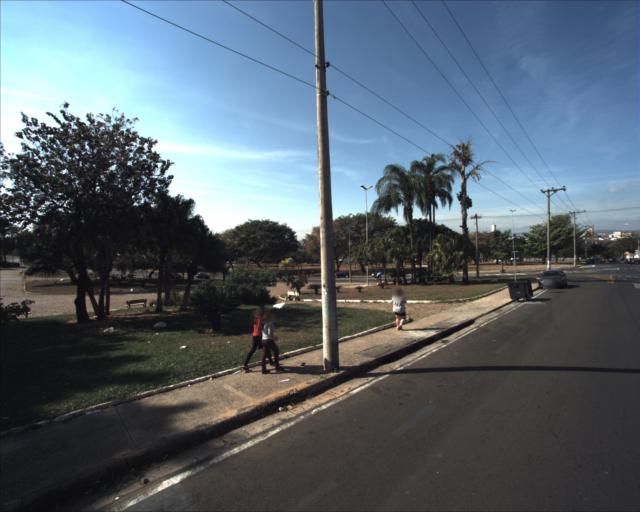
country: BR
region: Sao Paulo
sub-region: Sorocaba
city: Sorocaba
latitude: -23.4908
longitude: -47.4492
